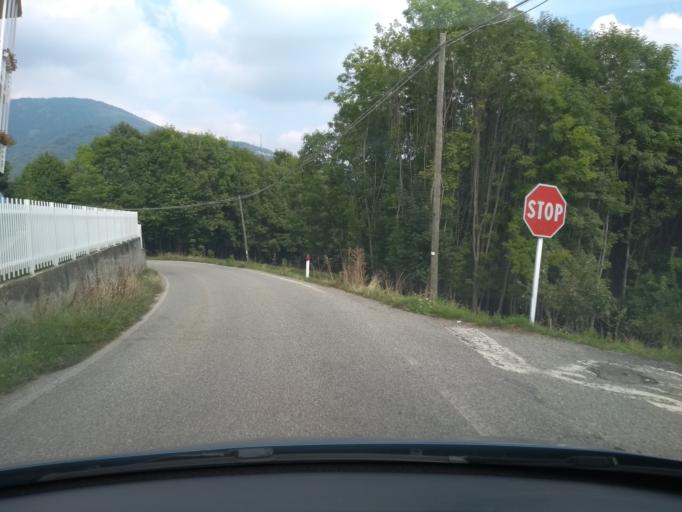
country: IT
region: Piedmont
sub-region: Provincia di Torino
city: Corio
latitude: 45.3118
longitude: 7.5202
